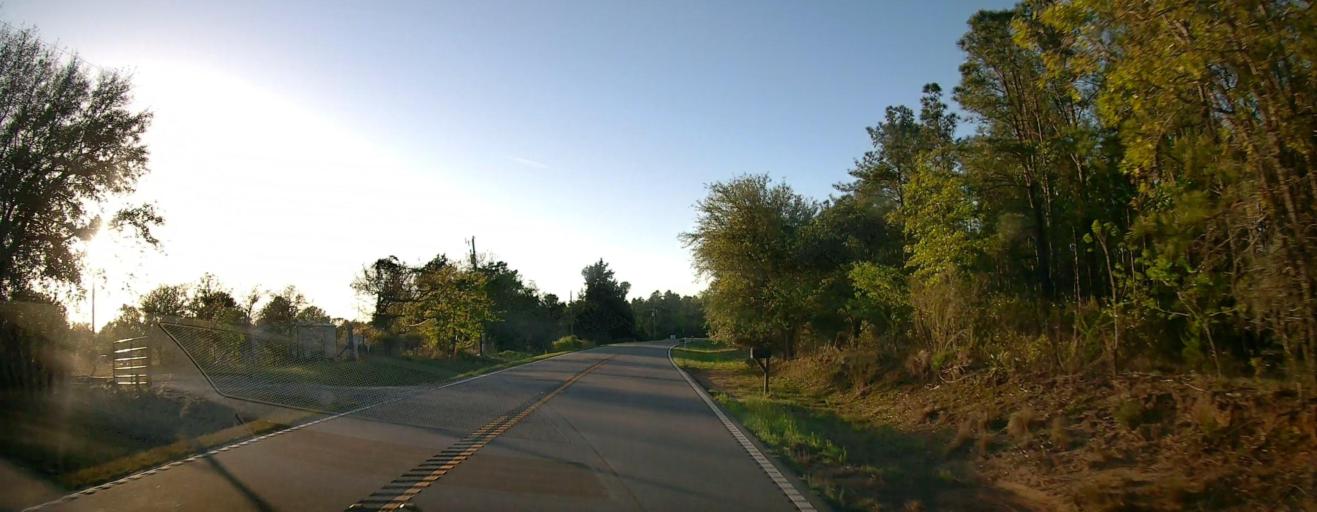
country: US
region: Georgia
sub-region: Marion County
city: Buena Vista
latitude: 32.4996
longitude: -84.4630
